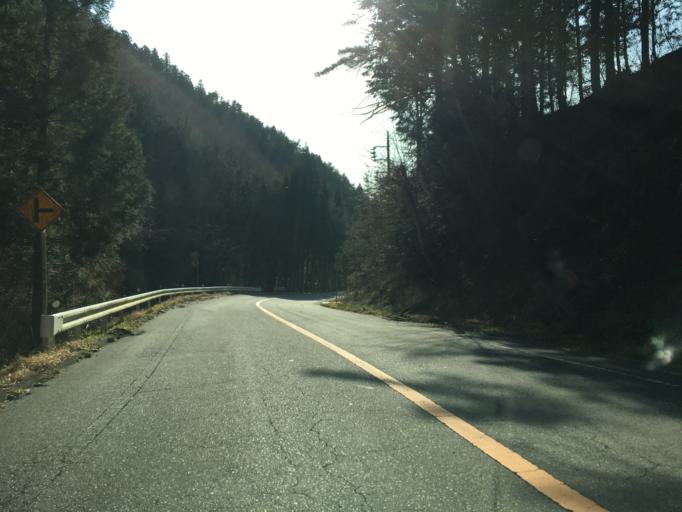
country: JP
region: Ibaraki
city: Daigo
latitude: 36.7359
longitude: 140.5202
